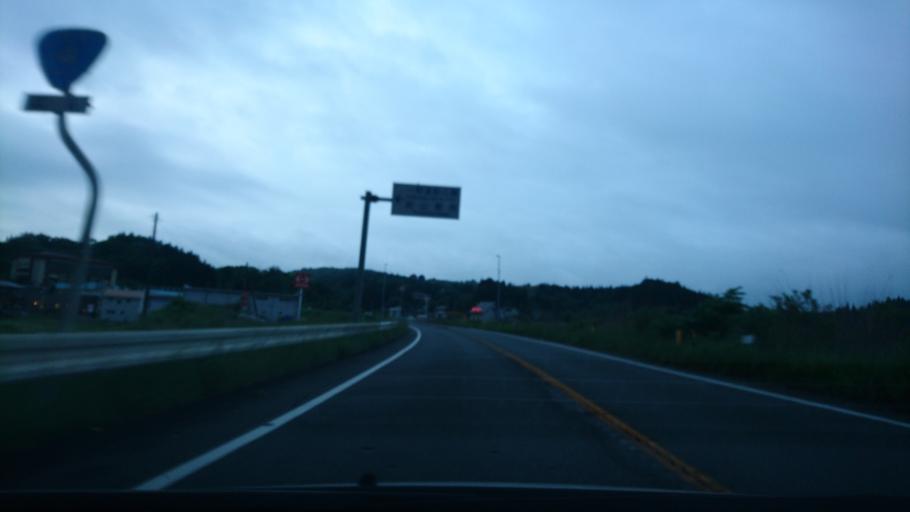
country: JP
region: Iwate
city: Ichinoseki
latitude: 38.9164
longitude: 141.1076
